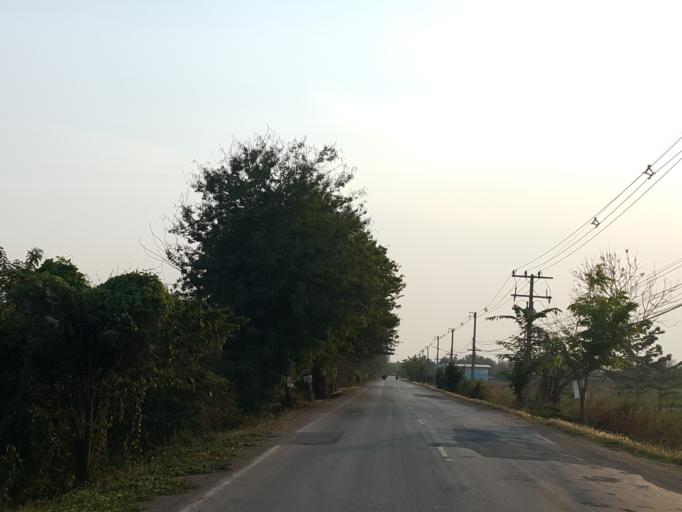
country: TH
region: Sukhothai
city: Si Samrong
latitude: 17.2149
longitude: 99.8802
